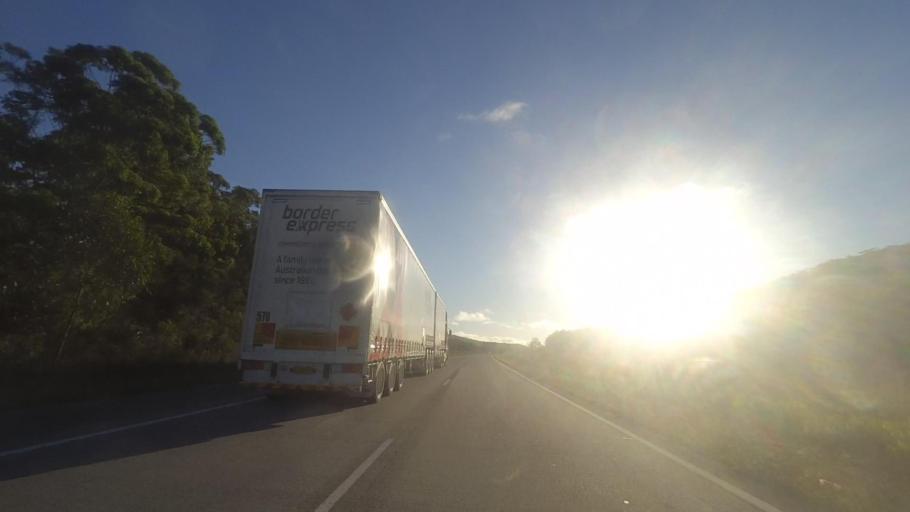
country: AU
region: New South Wales
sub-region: Great Lakes
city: Bulahdelah
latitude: -32.5199
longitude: 152.2045
